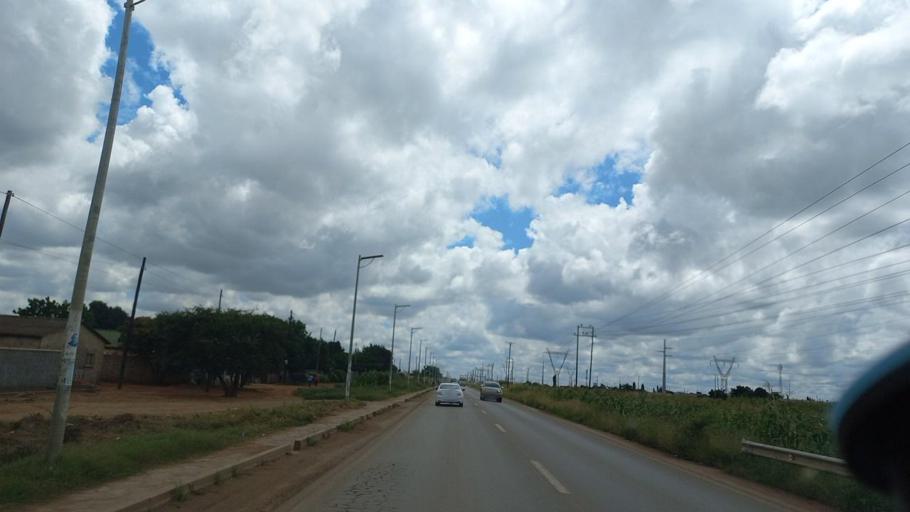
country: ZM
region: Lusaka
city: Lusaka
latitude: -15.4553
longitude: 28.3255
